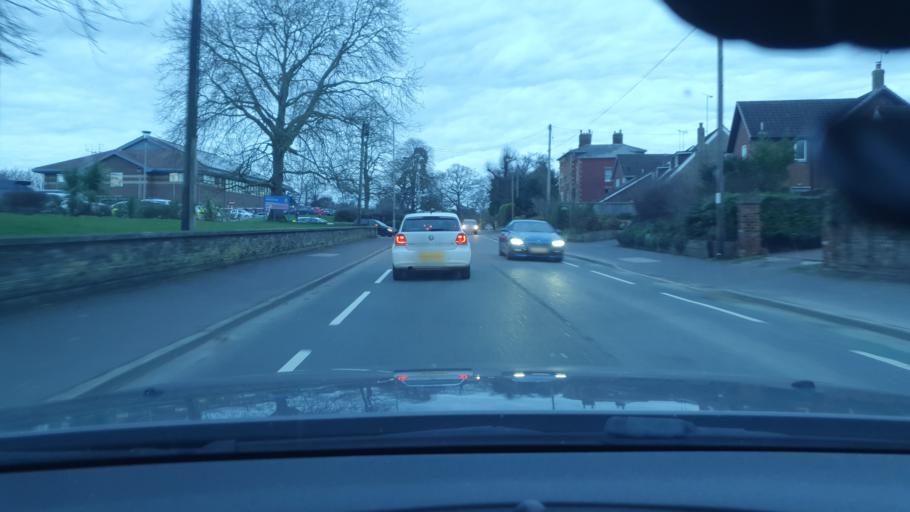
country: GB
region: England
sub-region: Wiltshire
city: Devizes
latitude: 51.3558
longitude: -1.9832
